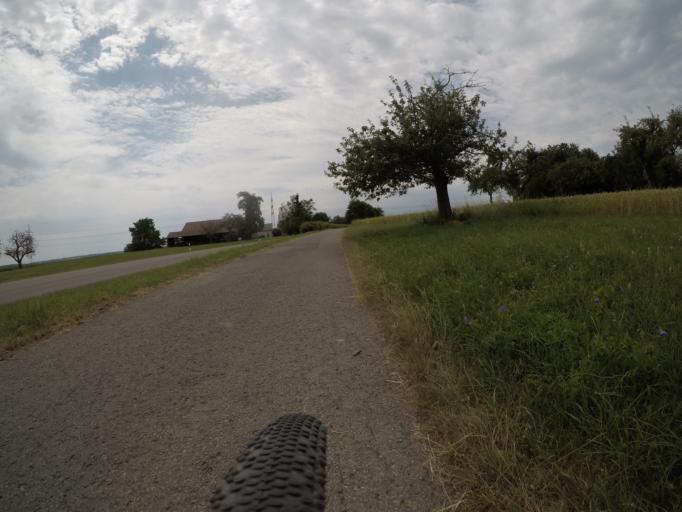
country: DE
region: Baden-Wuerttemberg
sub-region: Regierungsbezirk Stuttgart
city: Magstadt
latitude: 48.7175
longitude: 8.9544
